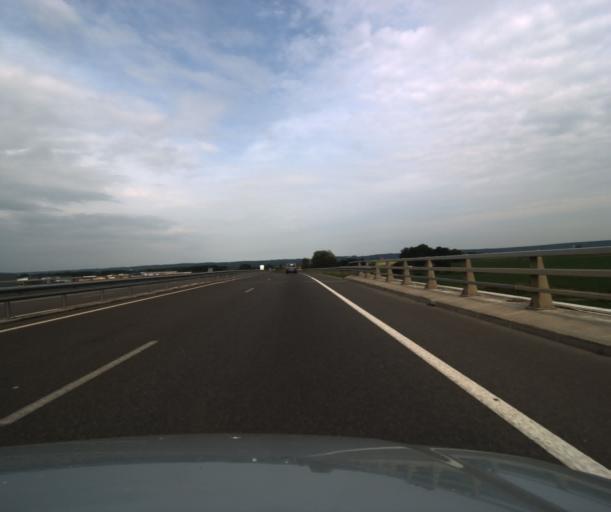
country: FR
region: Midi-Pyrenees
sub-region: Departement des Hautes-Pyrenees
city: Juillan
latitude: 43.2231
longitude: 0.0361
